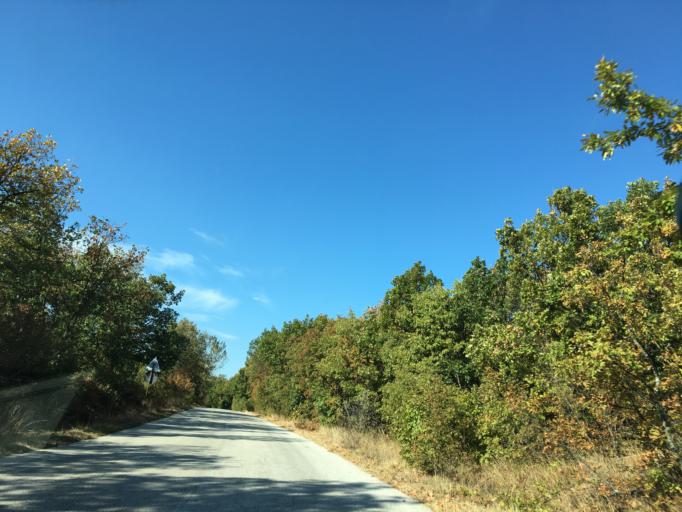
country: BG
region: Khaskovo
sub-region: Obshtina Ivaylovgrad
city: Ivaylovgrad
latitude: 41.5210
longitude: 26.0311
